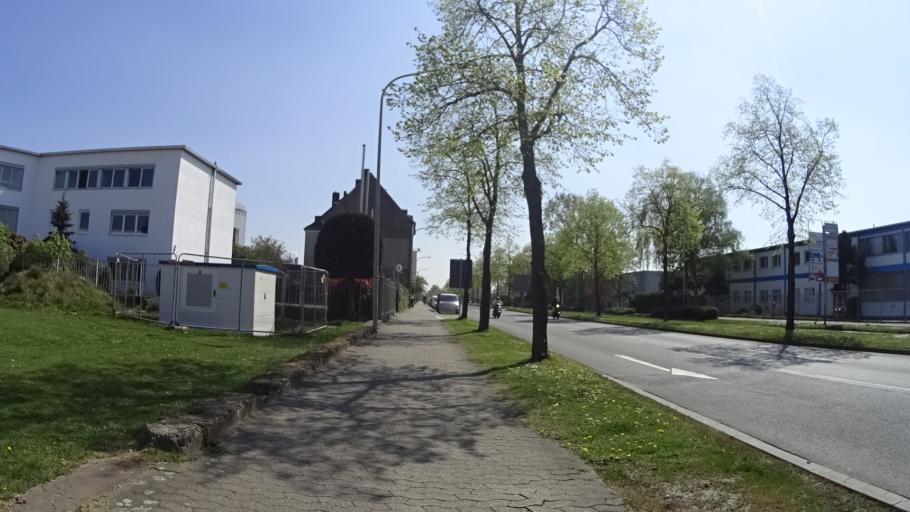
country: DE
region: North Rhine-Westphalia
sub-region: Regierungsbezirk Dusseldorf
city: Krefeld
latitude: 51.3446
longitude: 6.6567
